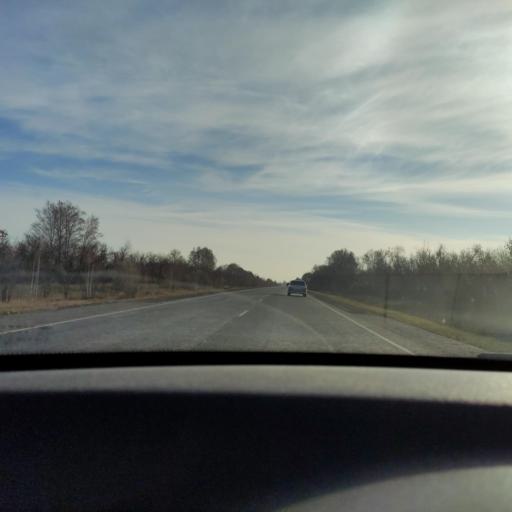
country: RU
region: Samara
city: Krasnoarmeyskoye
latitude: 52.7603
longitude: 50.0263
